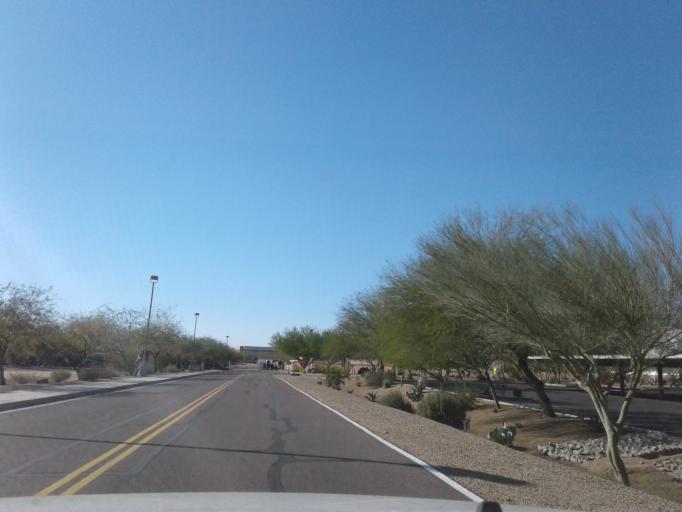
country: US
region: Arizona
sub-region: Maricopa County
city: Paradise Valley
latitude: 33.6548
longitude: -111.9556
